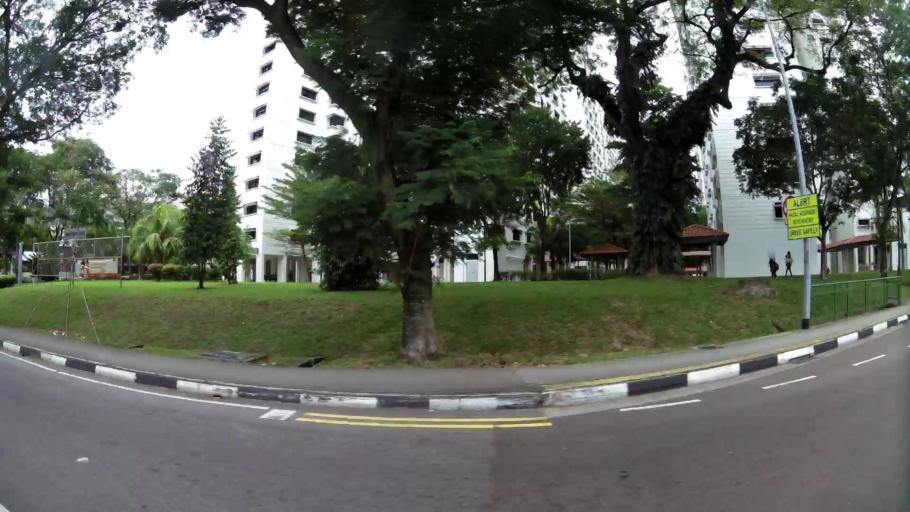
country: SG
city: Singapore
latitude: 1.3335
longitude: 103.7203
